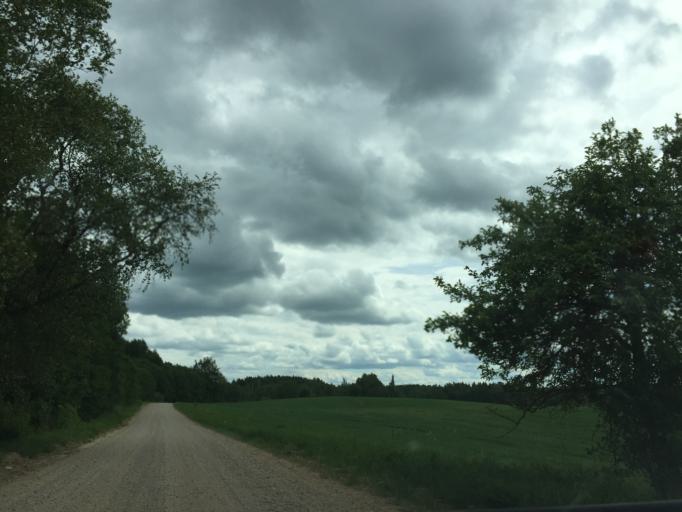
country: LV
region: Dagda
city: Dagda
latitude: 56.0564
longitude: 27.6491
